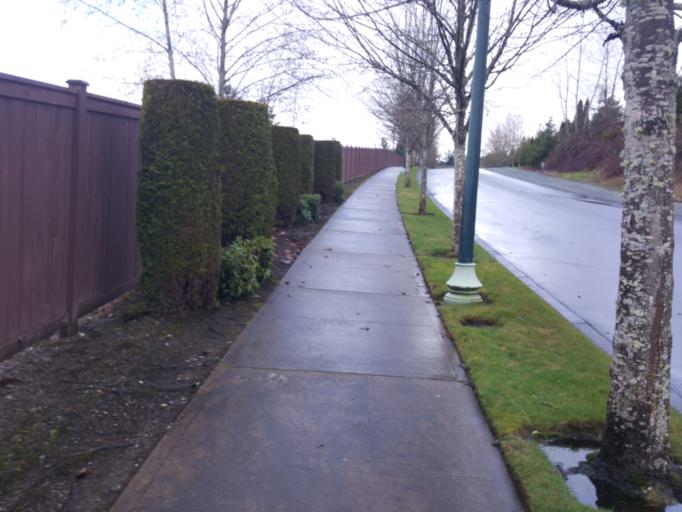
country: US
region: Washington
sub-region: Pierce County
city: Lakewood
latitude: 47.2006
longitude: -122.5247
